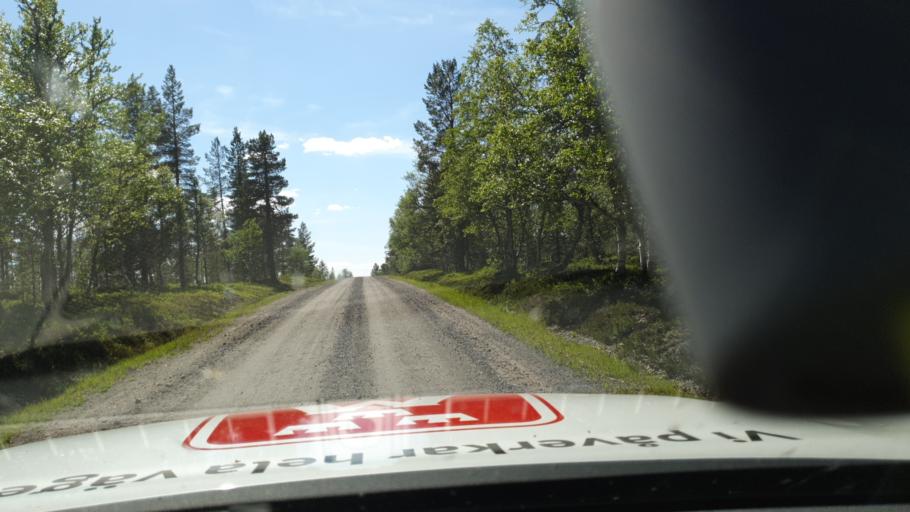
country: NO
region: Hedmark
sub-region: Engerdal
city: Engerdal
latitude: 62.1396
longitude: 12.9393
